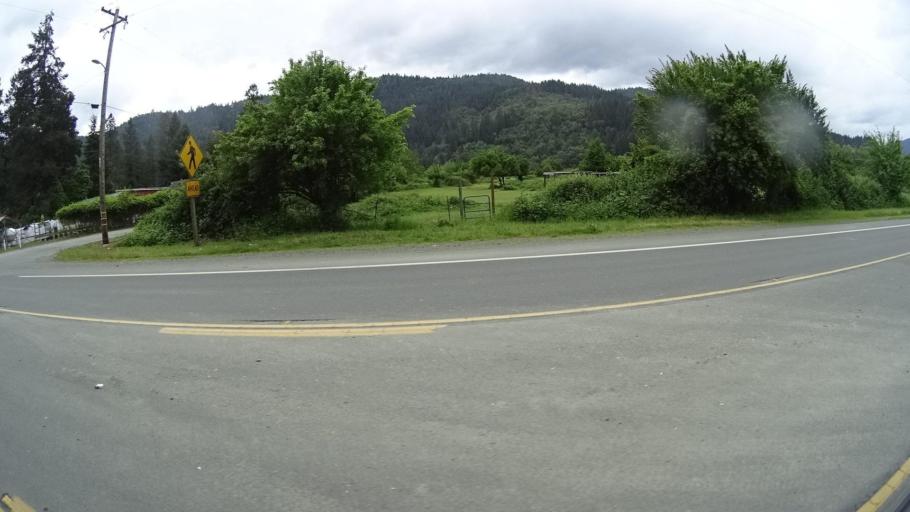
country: US
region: California
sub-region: Humboldt County
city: Willow Creek
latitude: 41.0671
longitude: -123.6864
